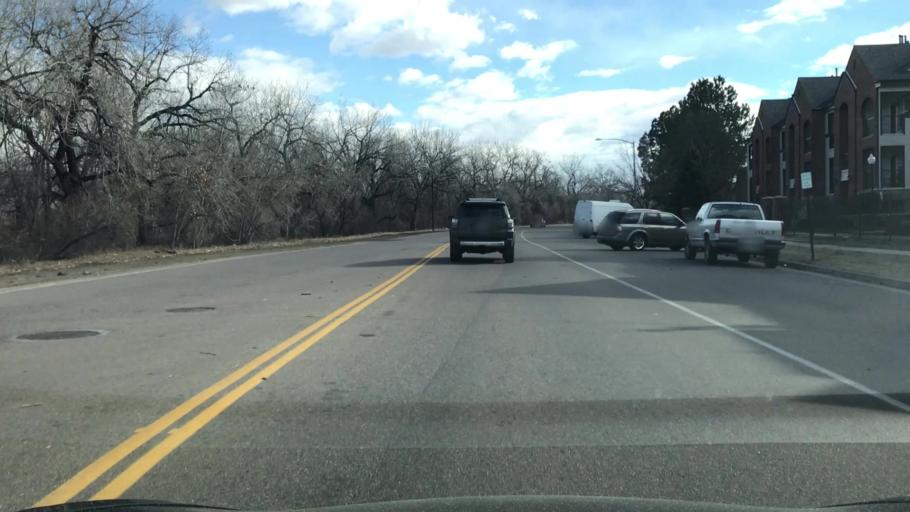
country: US
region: Colorado
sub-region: Arapahoe County
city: Glendale
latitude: 39.7031
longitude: -104.9311
